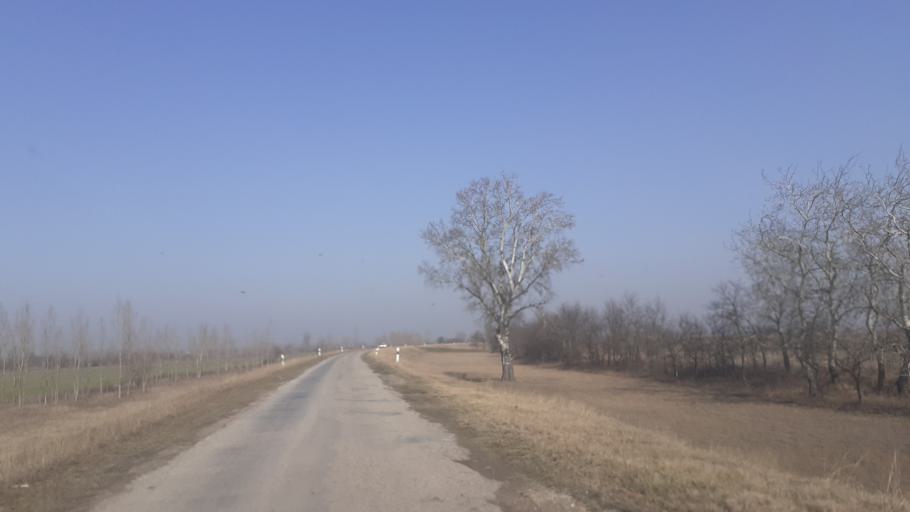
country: HU
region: Bacs-Kiskun
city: Tass
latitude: 47.0440
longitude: 18.9931
